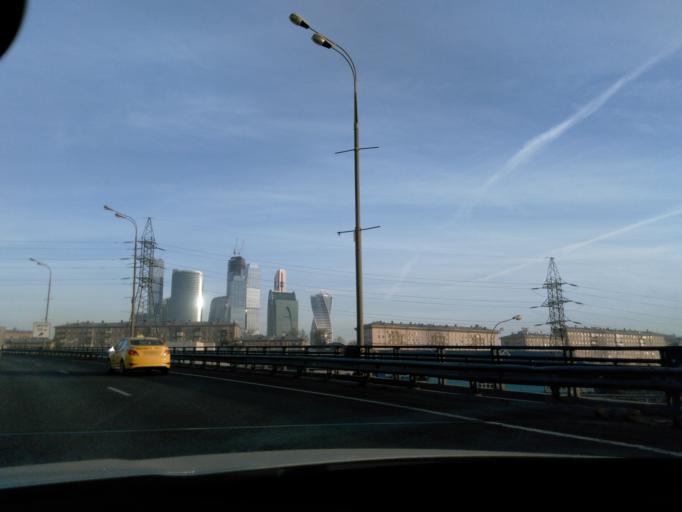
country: RU
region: Moskovskaya
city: Presnenskiy
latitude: 55.7345
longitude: 37.5427
